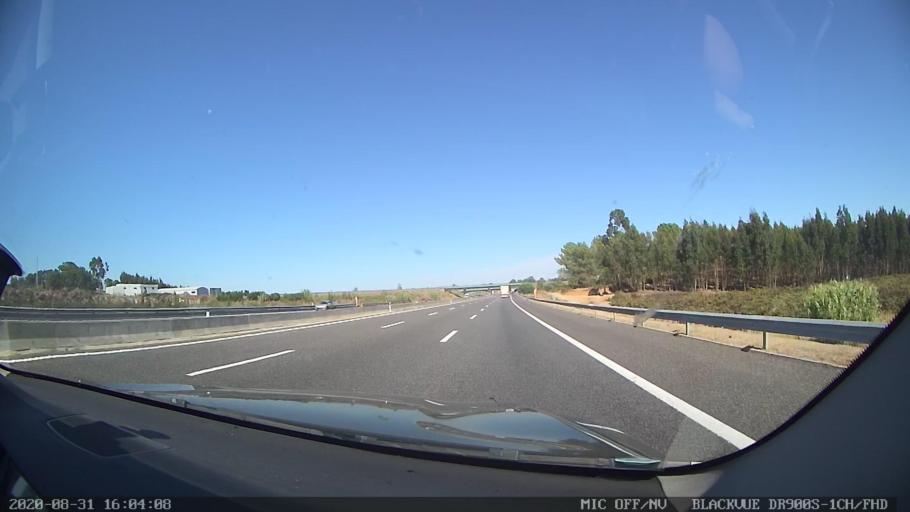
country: PT
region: Lisbon
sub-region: Azambuja
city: Aveiras de Cima
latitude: 39.1517
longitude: -8.8749
